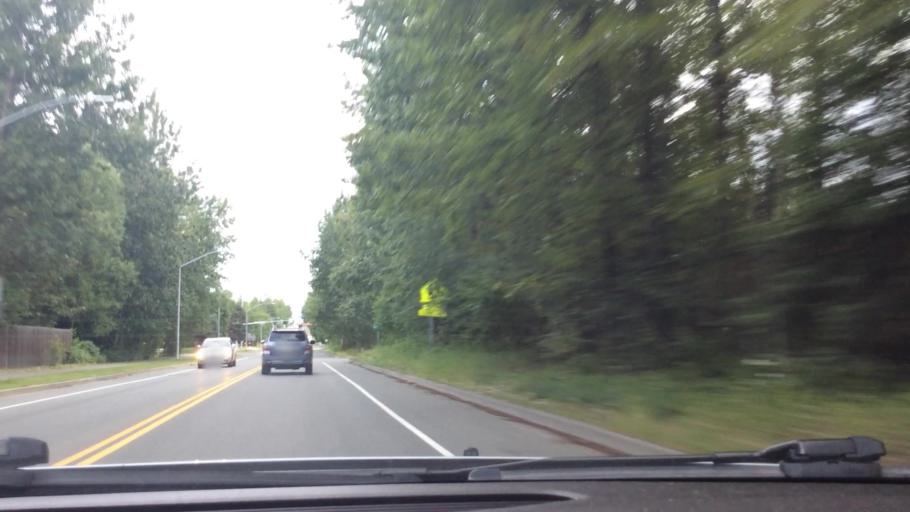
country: US
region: Alaska
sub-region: Anchorage Municipality
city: Anchorage
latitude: 61.1975
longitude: -149.7634
